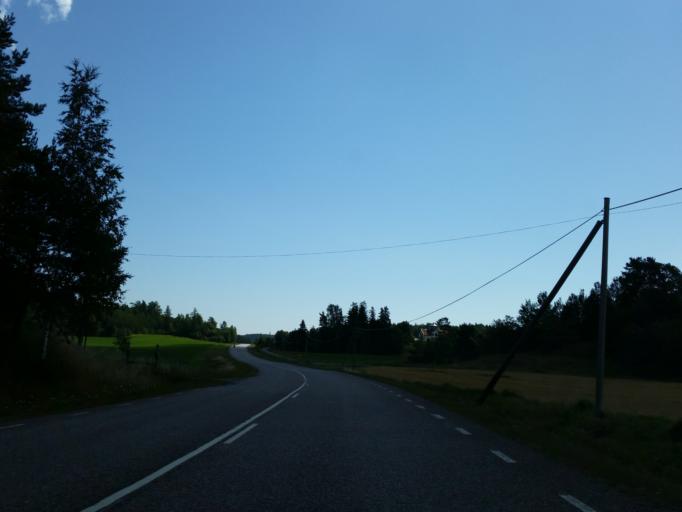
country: SE
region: Soedermanland
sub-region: Trosa Kommun
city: Vagnharad
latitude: 59.0007
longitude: 17.6040
